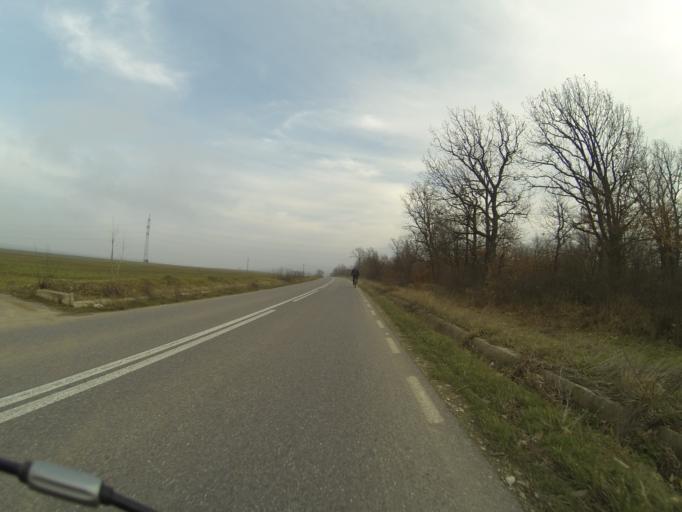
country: RO
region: Mehedinti
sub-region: Comuna Corlatel
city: Corlatel
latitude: 44.4009
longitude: 22.9086
